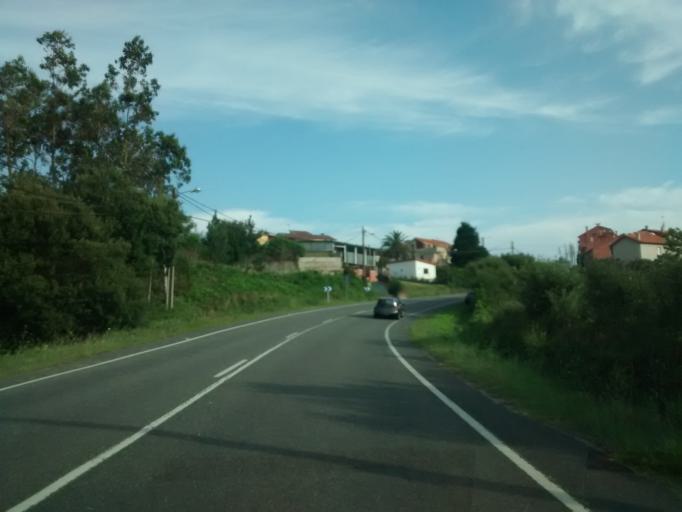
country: ES
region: Galicia
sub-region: Provincia de Pontevedra
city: Sanxenxo
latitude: 42.3947
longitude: -8.8440
